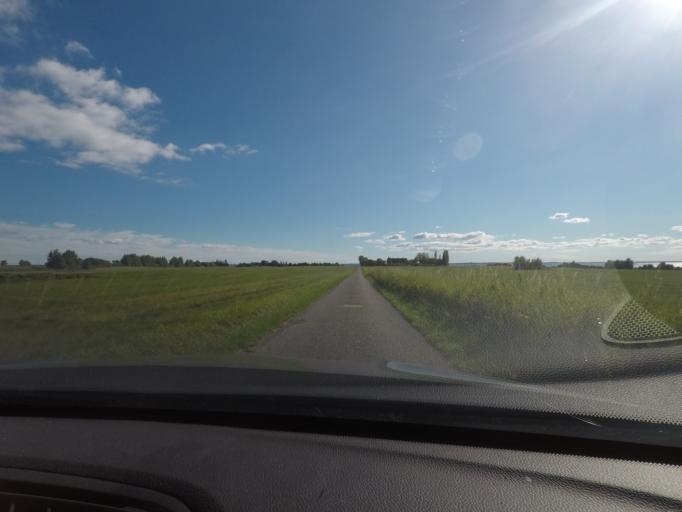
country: DK
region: Zealand
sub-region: Guldborgsund Kommune
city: Sakskobing
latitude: 54.9650
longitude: 11.5310
